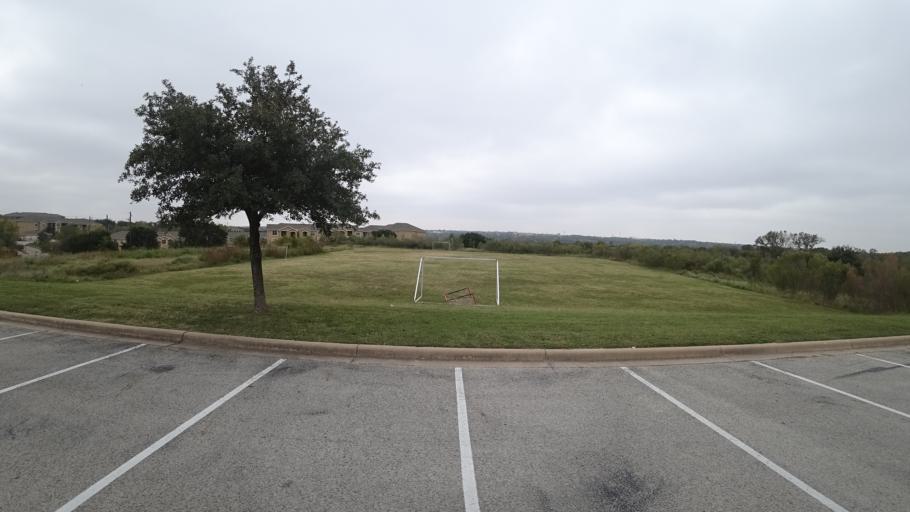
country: US
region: Texas
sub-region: Travis County
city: Pflugerville
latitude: 30.3832
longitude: -97.6541
